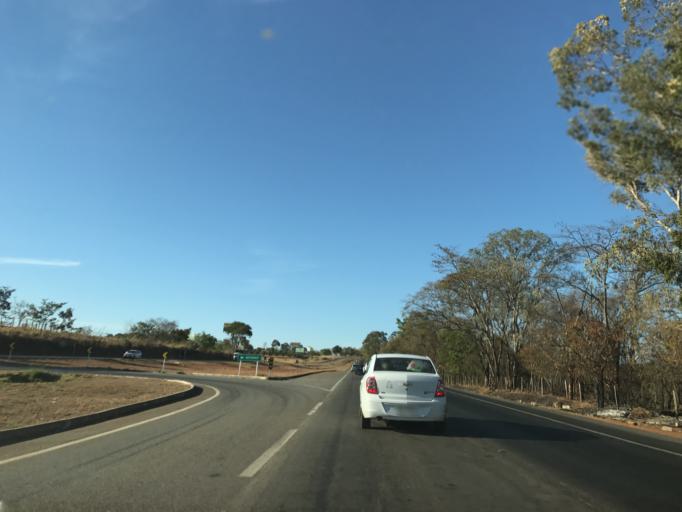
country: BR
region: Goias
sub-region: Hidrolandia
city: Hidrolandia
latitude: -16.9249
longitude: -49.2523
